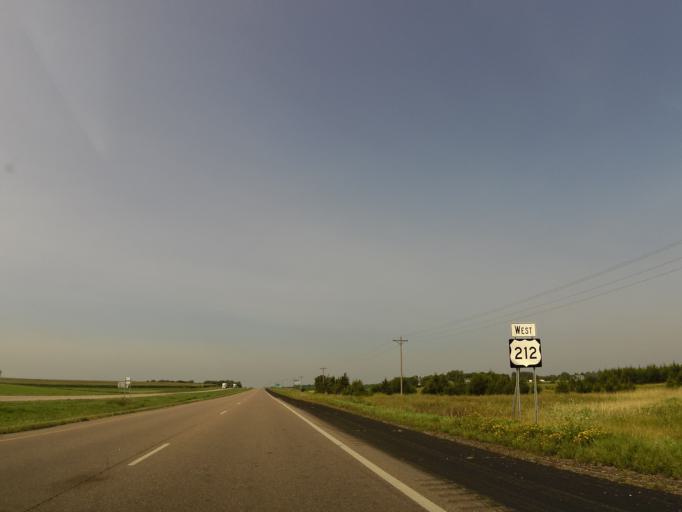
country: US
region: Minnesota
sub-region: Carver County
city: Norwood (historical)
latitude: 44.7684
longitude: -93.9804
